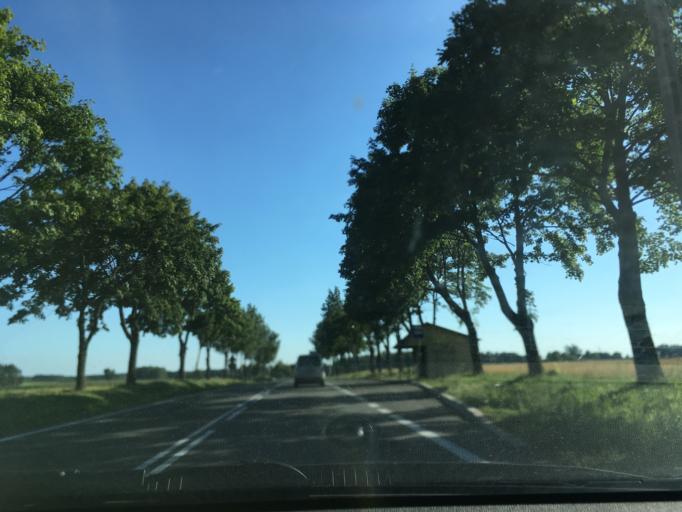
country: PL
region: Podlasie
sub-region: Powiat sokolski
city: Janow
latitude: 53.3916
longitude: 23.1137
